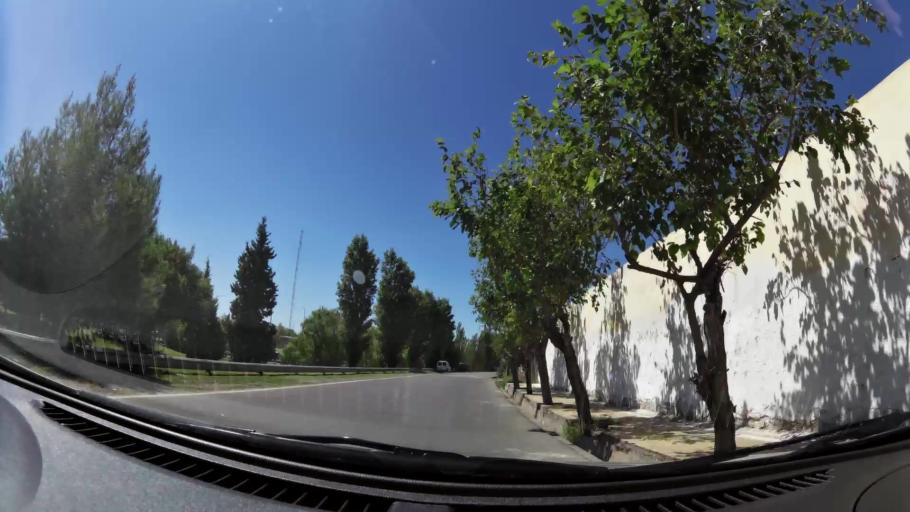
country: AR
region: San Juan
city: San Juan
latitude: -31.5243
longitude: -68.5523
